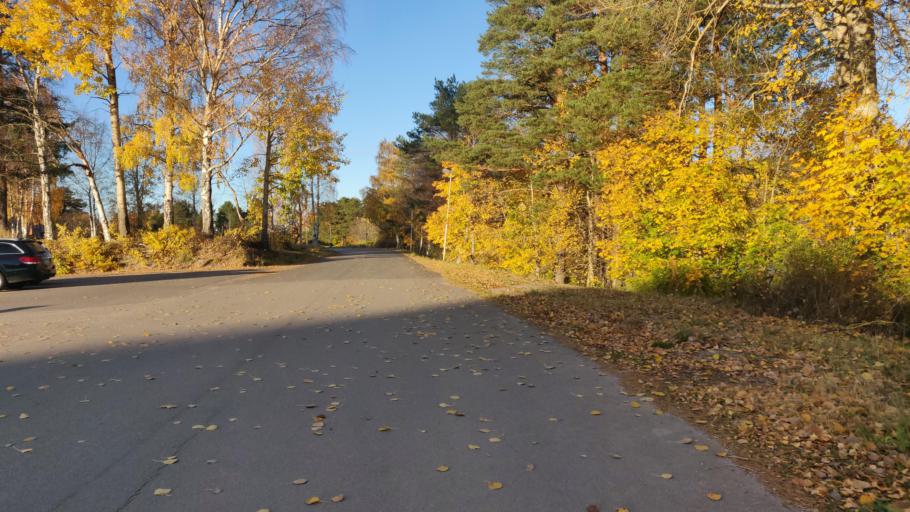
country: SE
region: Vaesternorrland
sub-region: Sundsvalls Kommun
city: Skottsund
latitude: 62.2972
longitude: 17.3837
